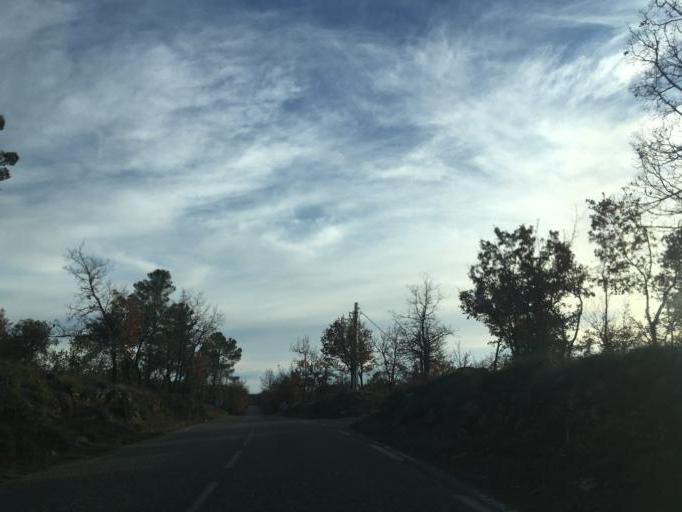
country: FR
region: Provence-Alpes-Cote d'Azur
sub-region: Departement du Var
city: Aups
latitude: 43.6122
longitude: 6.2183
